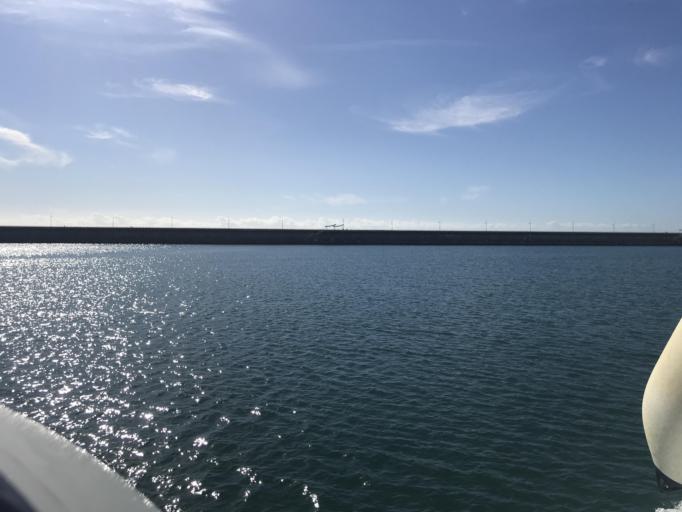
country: ES
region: Valencia
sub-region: Provincia de Alicante
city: Torrevieja
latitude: 37.9688
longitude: -0.6864
